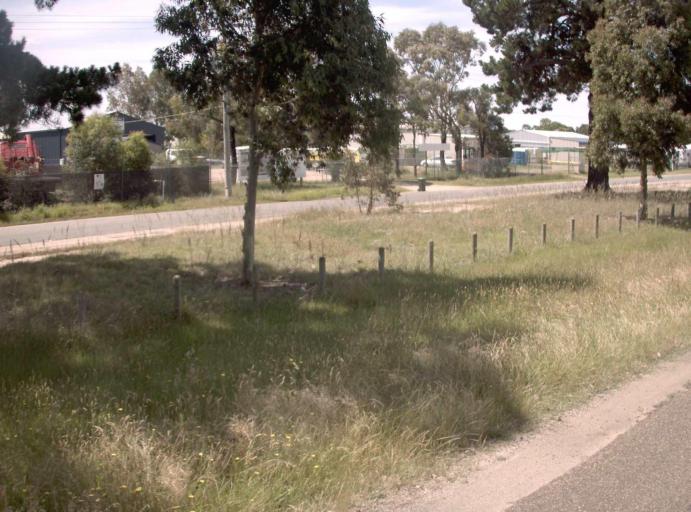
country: AU
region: Victoria
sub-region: Wellington
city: Sale
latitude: -37.9635
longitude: 147.0872
